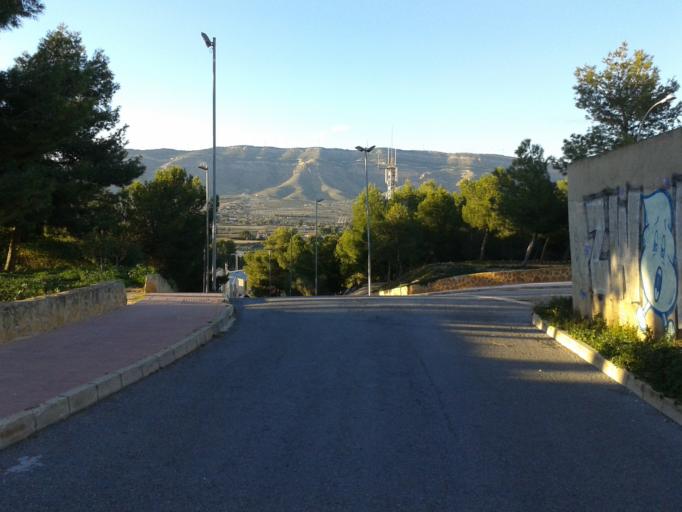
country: ES
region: Castille-La Mancha
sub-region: Provincia de Albacete
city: Caudete
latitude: 38.7050
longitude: -0.9915
